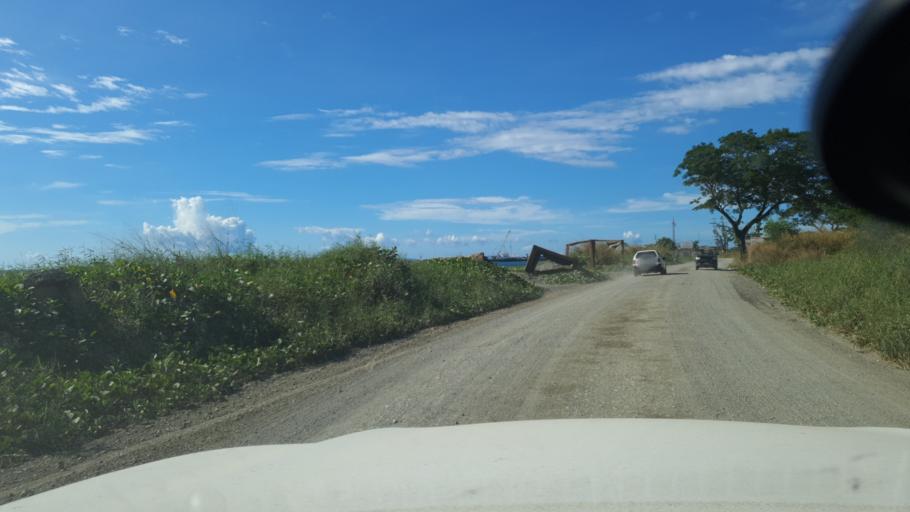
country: SB
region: Guadalcanal
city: Honiara
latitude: -9.4155
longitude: 160.0149
